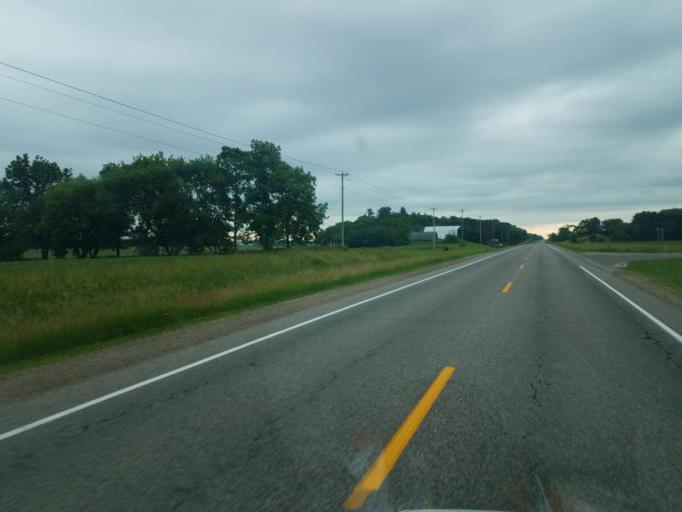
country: US
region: Wisconsin
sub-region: Juneau County
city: Mauston
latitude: 43.7891
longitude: -90.1577
